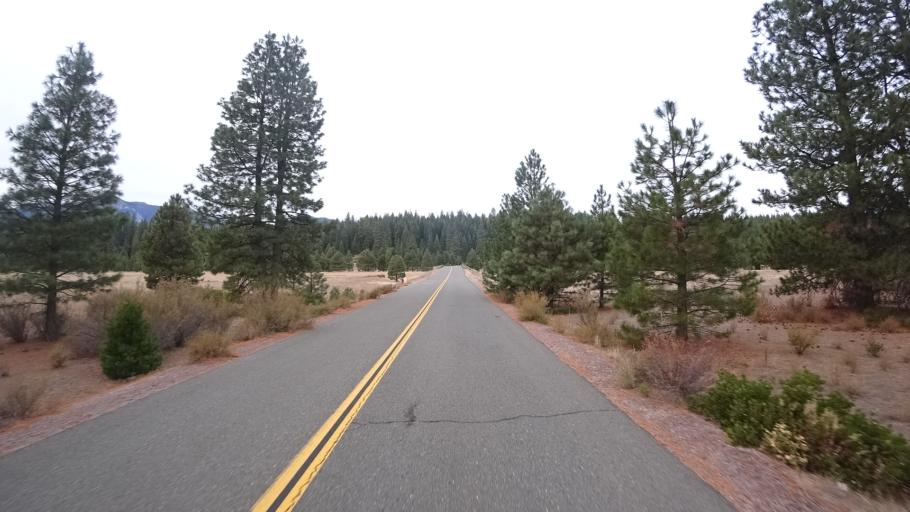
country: US
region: California
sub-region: Siskiyou County
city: Weed
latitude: 41.3945
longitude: -122.3874
